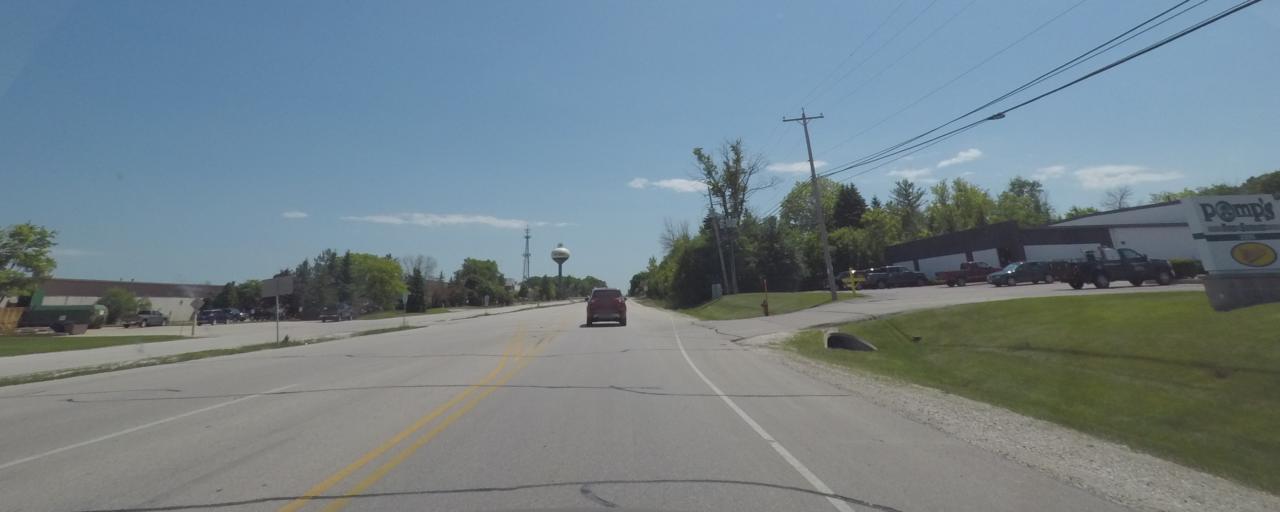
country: US
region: Wisconsin
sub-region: Waukesha County
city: New Berlin
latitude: 43.0019
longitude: -88.1276
